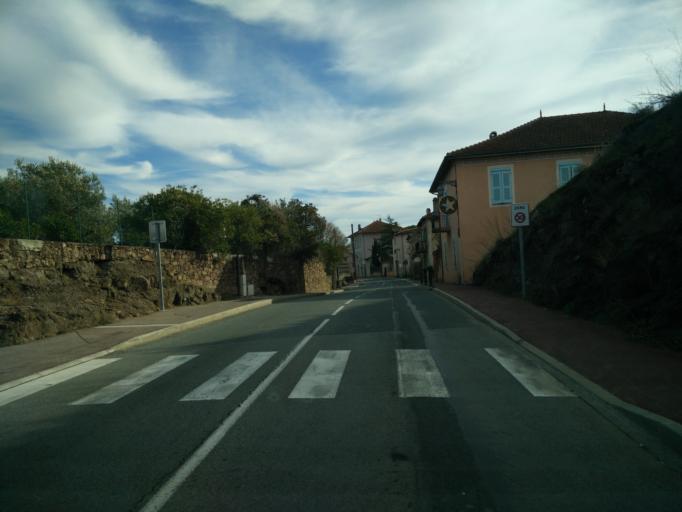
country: FR
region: Provence-Alpes-Cote d'Azur
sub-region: Departement du Var
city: Roquebrune-sur-Argens
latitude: 43.4469
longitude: 6.6341
